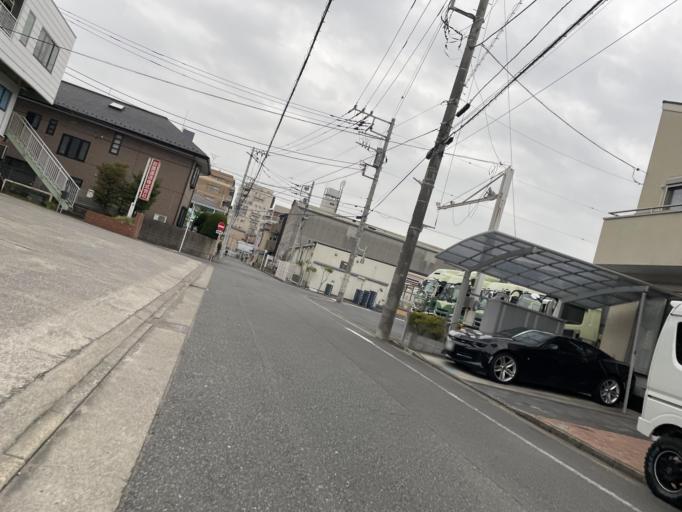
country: JP
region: Tokyo
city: Urayasu
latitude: 35.6741
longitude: 139.8641
